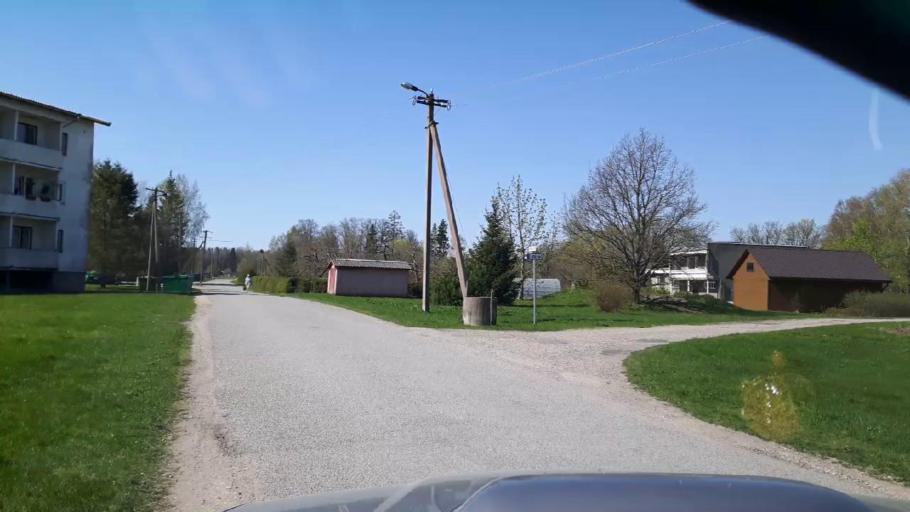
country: EE
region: Paernumaa
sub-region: Tootsi vald
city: Tootsi
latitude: 58.4781
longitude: 24.8037
